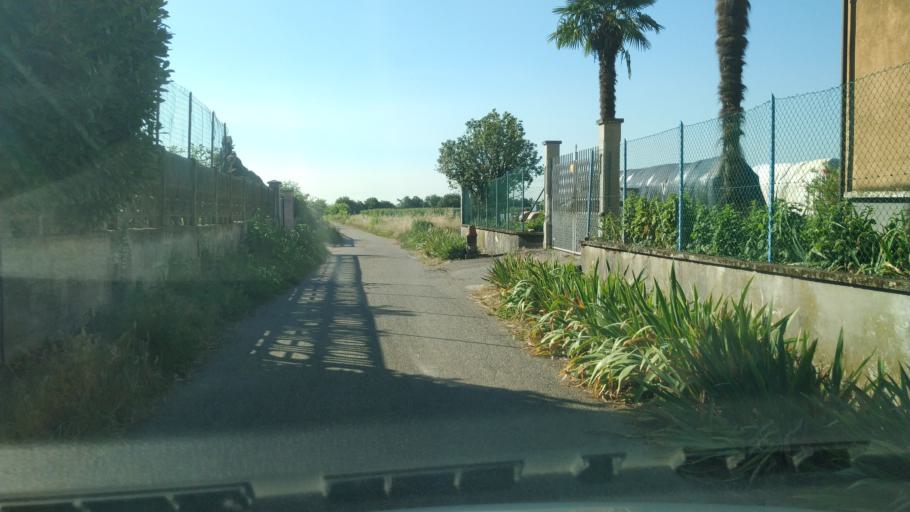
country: IT
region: Piedmont
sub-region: Provincia di Vercelli
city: Alice Castello
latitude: 45.3602
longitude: 8.0757
